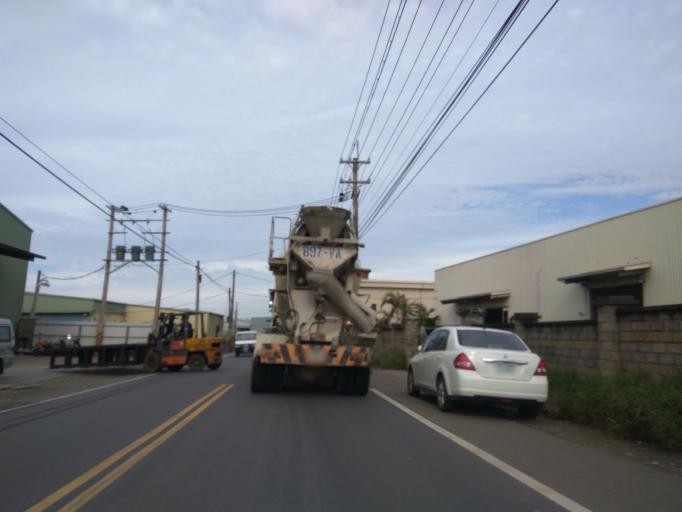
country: TW
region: Taiwan
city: Daxi
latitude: 24.9407
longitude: 121.1587
